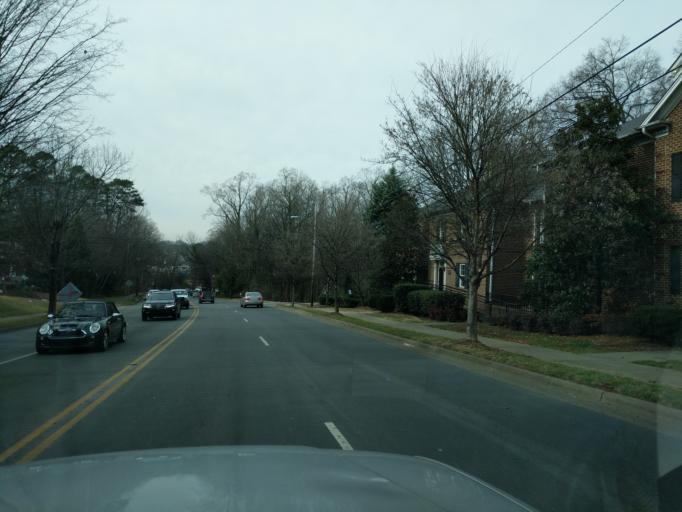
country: US
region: North Carolina
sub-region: Mecklenburg County
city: Charlotte
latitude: 35.1711
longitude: -80.8417
